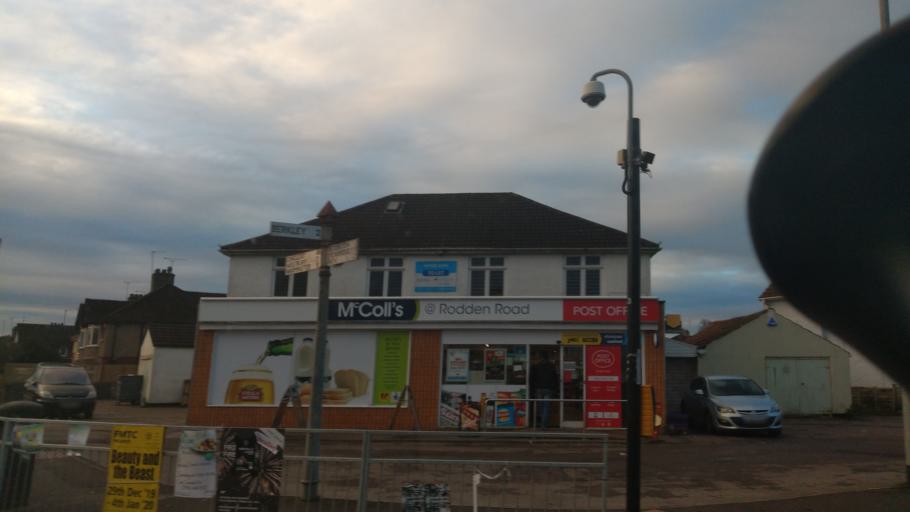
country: GB
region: England
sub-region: Somerset
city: Frome
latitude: 51.2350
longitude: -2.3132
